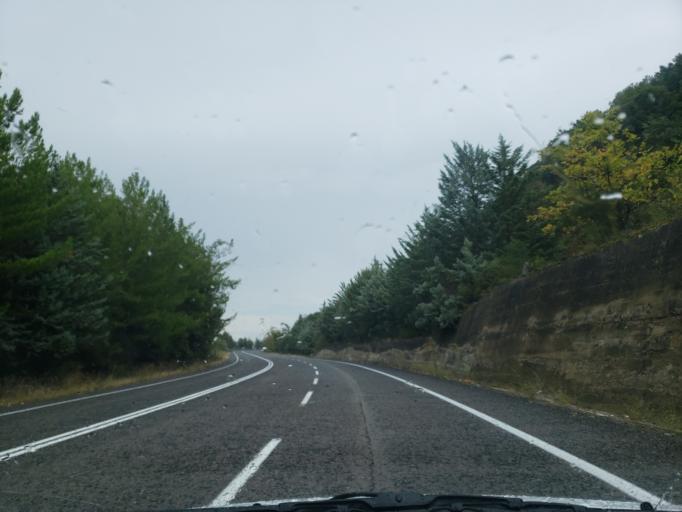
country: GR
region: Central Greece
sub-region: Nomos Fthiotidos
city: Anthili
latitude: 38.7888
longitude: 22.4863
